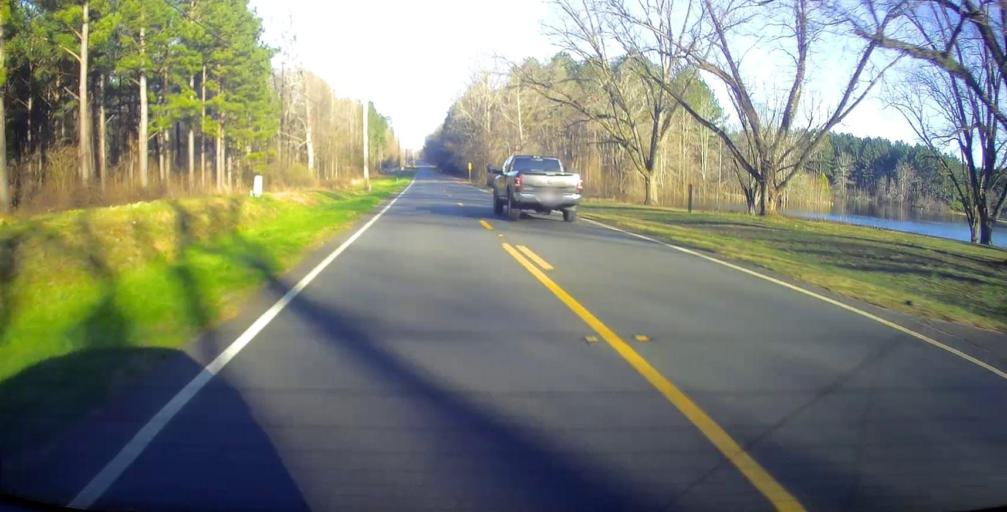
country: US
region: Georgia
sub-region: Harris County
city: Pine Mountain
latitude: 32.9162
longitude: -84.7857
